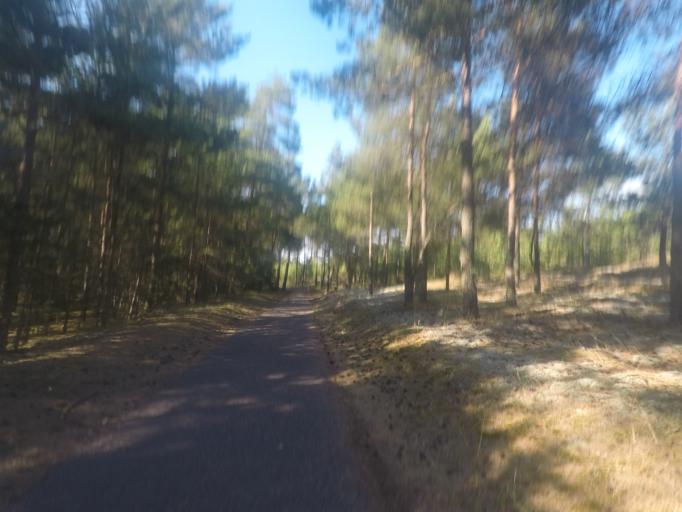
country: LT
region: Klaipedos apskritis
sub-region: Klaipeda
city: Klaipeda
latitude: 55.5665
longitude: 21.1121
